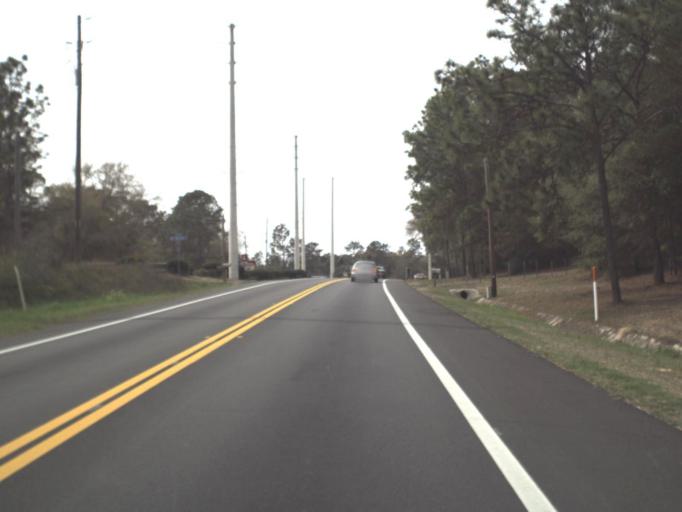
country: US
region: Florida
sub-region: Leon County
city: Tallahassee
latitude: 30.4362
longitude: -84.3774
